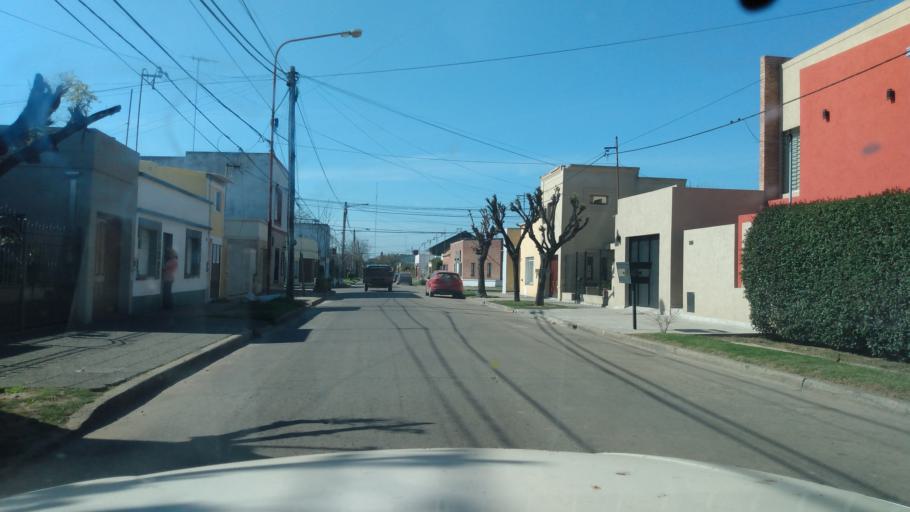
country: AR
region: Buenos Aires
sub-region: Partido de Lujan
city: Lujan
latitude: -34.5699
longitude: -59.0995
